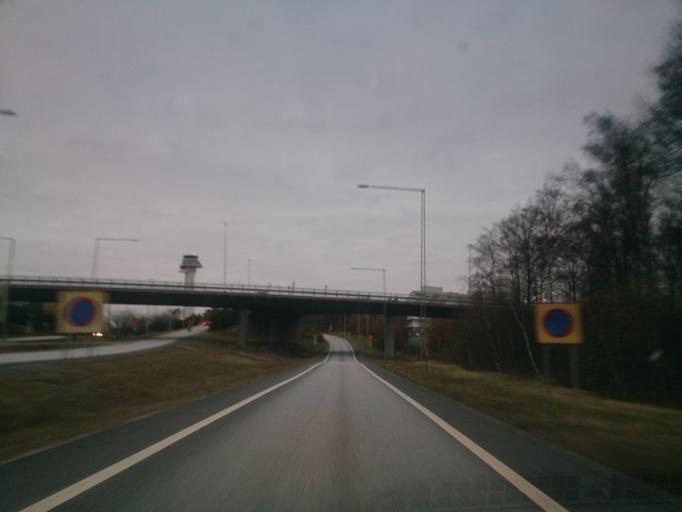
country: SE
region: Stockholm
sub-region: Sigtuna Kommun
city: Rosersberg
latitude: 59.6441
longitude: 17.9370
